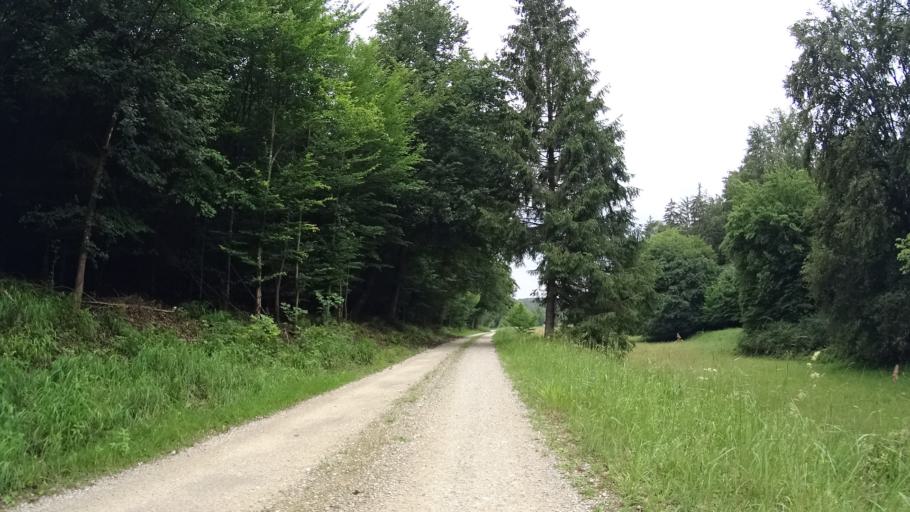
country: DE
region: Bavaria
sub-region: Upper Bavaria
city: Denkendorf
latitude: 48.9154
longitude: 11.5367
